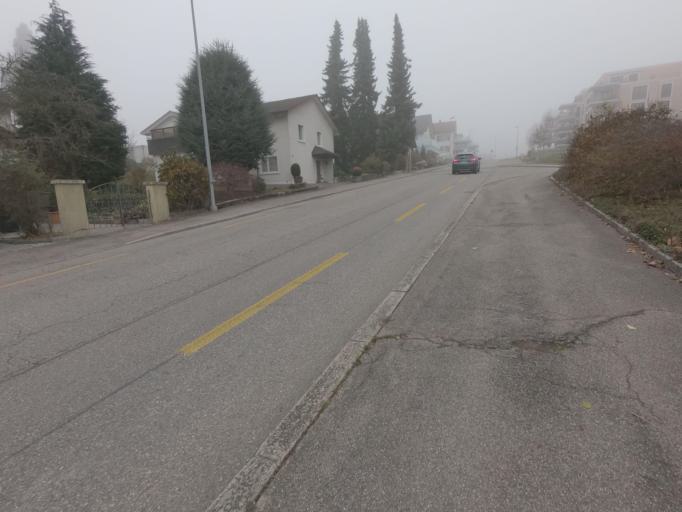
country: CH
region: Solothurn
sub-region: Bezirk Lebern
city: Grenchen
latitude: 47.1974
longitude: 7.4064
